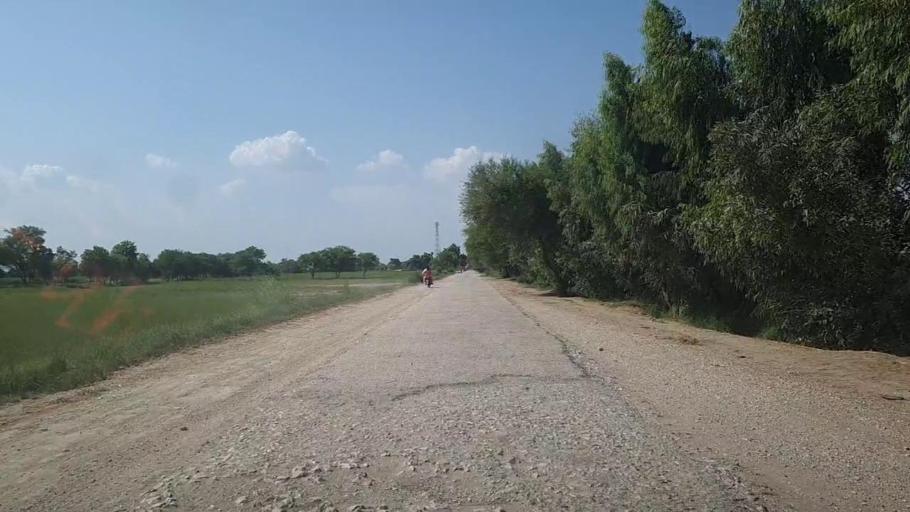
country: PK
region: Sindh
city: Khairpur
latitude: 28.1154
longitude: 69.6181
